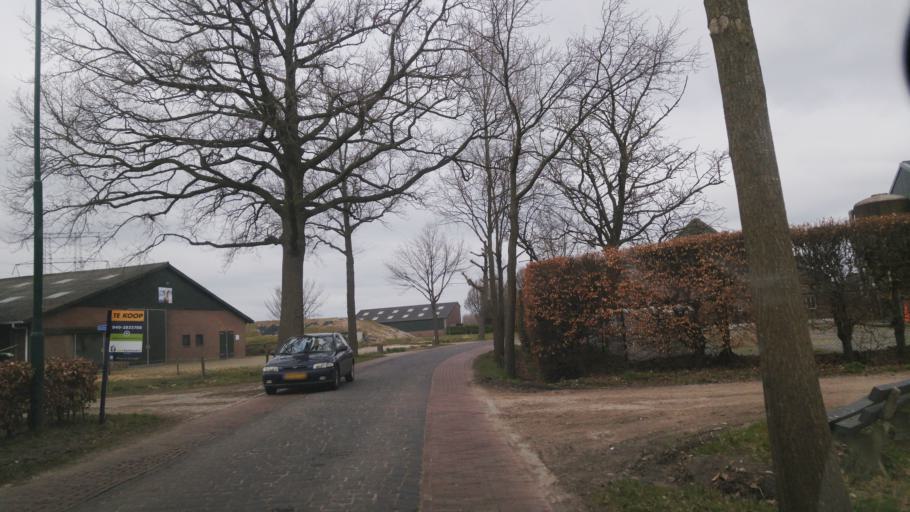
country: NL
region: North Brabant
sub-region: Gemeente Eindhoven
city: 't Hofke
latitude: 51.4781
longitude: 5.5167
